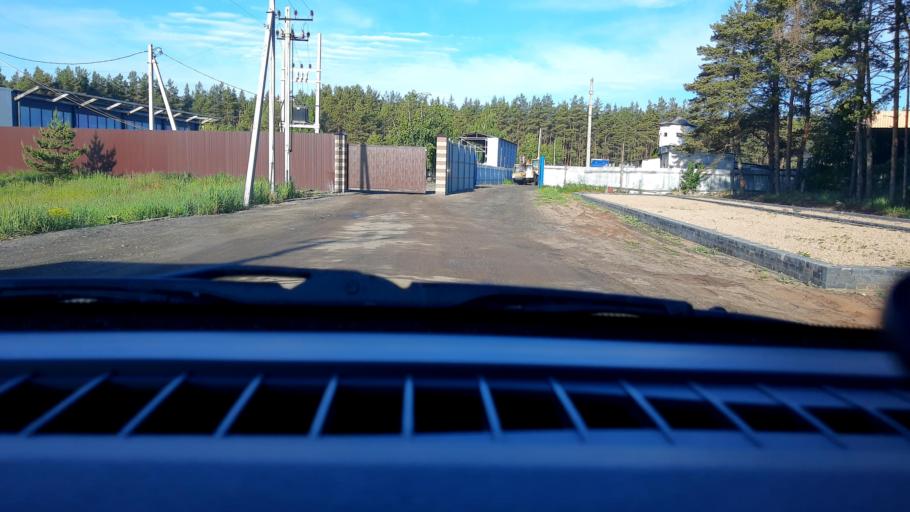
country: RU
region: Nizjnij Novgorod
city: Gorbatovka
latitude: 56.3047
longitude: 43.7391
